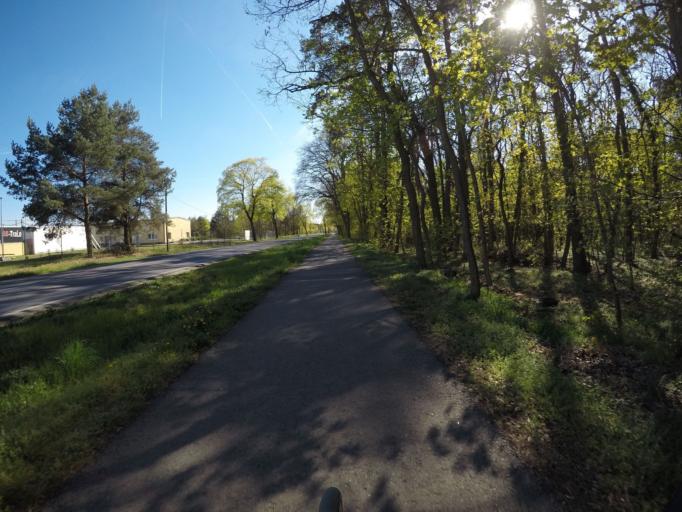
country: DE
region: Brandenburg
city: Rehfelde
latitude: 52.4940
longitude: 13.9184
